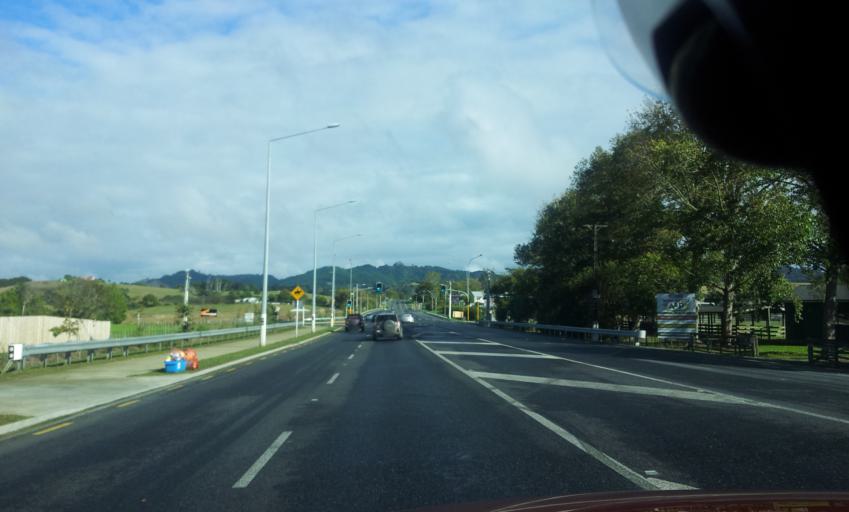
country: NZ
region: Auckland
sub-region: Auckland
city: Warkworth
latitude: -36.3925
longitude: 174.6528
